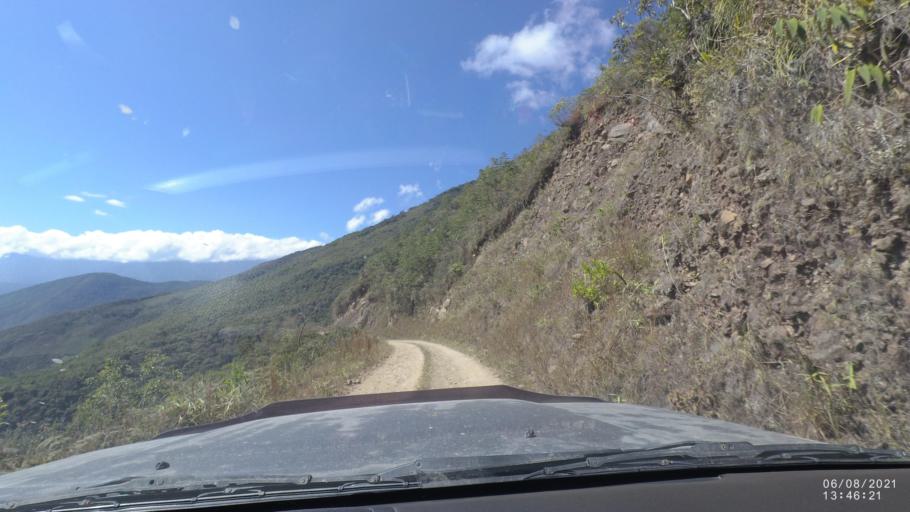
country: BO
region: La Paz
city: Quime
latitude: -16.6692
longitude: -66.7283
